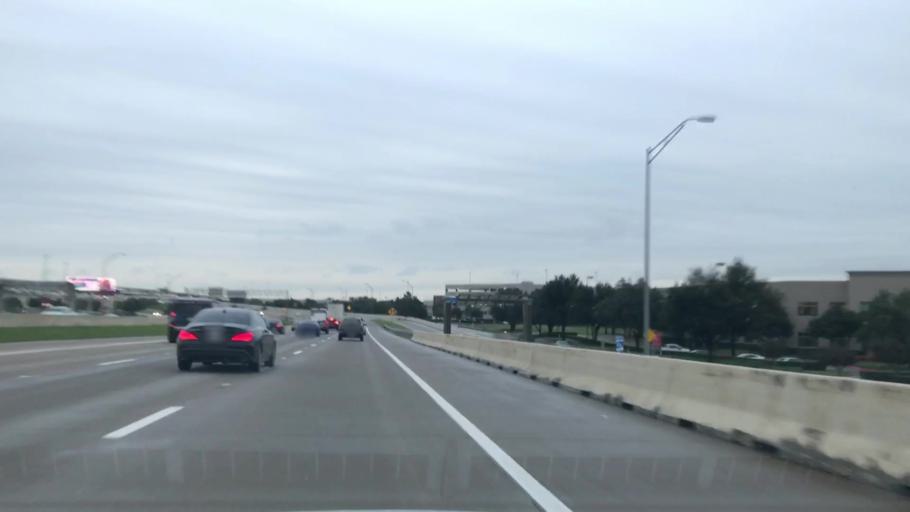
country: US
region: Texas
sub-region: Denton County
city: Lewisville
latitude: 32.9931
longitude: -96.9712
